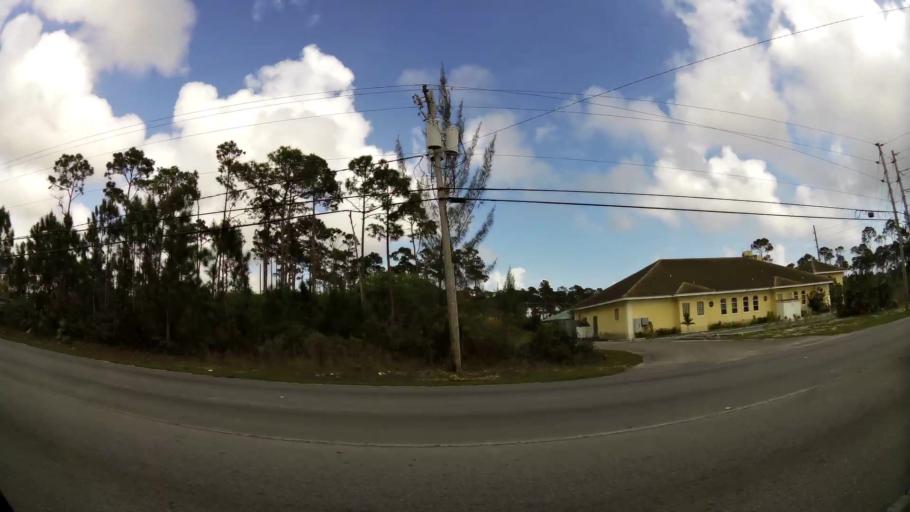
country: BS
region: Freeport
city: Freeport
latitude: 26.5233
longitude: -78.6986
